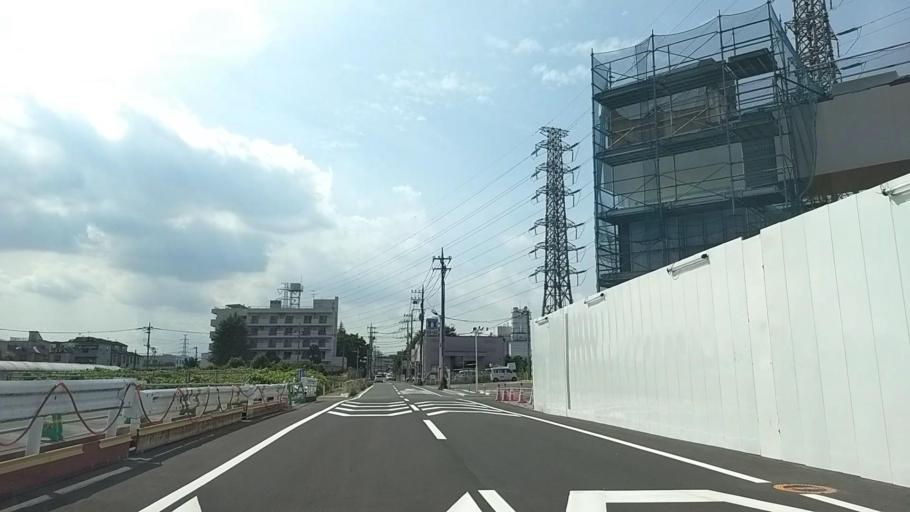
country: JP
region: Kanagawa
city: Yokohama
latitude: 35.5168
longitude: 139.5851
